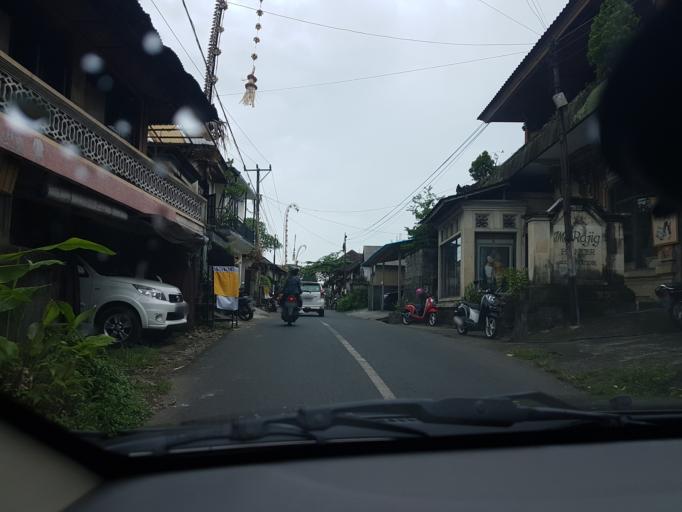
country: ID
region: Bali
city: Banjar Pande
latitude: -8.5070
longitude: 115.2484
